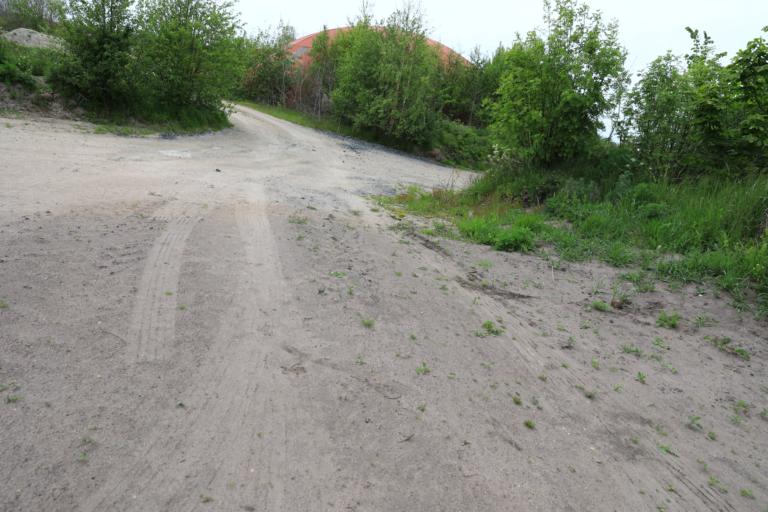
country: SE
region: Halland
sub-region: Varbergs Kommun
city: Varberg
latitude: 57.1488
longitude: 12.2345
